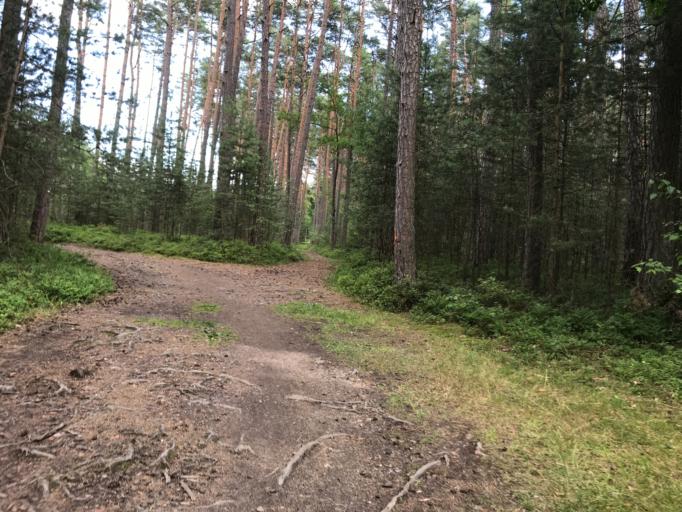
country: CZ
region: Jihocesky
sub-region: Okres Jindrichuv Hradec
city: Trebon
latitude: 48.9875
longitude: 14.7274
